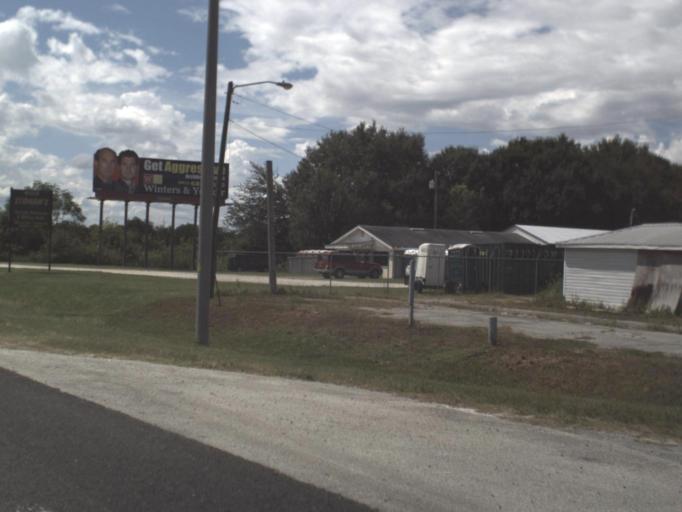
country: US
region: Florida
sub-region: Polk County
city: Lake Wales
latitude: 27.9032
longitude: -81.6299
